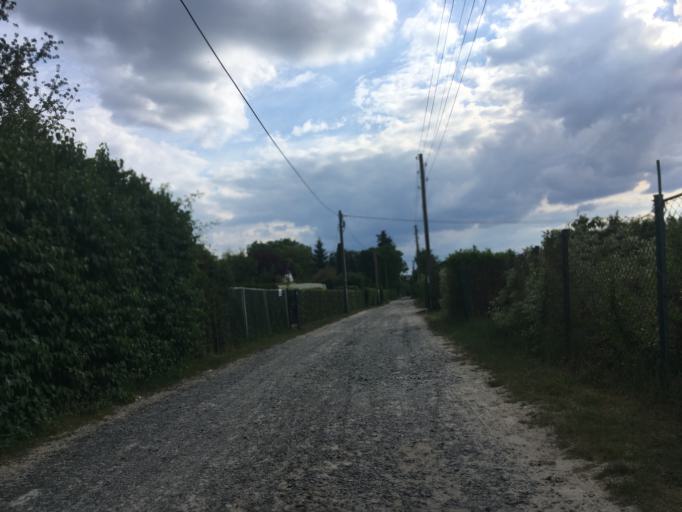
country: DE
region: Berlin
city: Johannisthal
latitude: 52.4431
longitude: 13.4884
